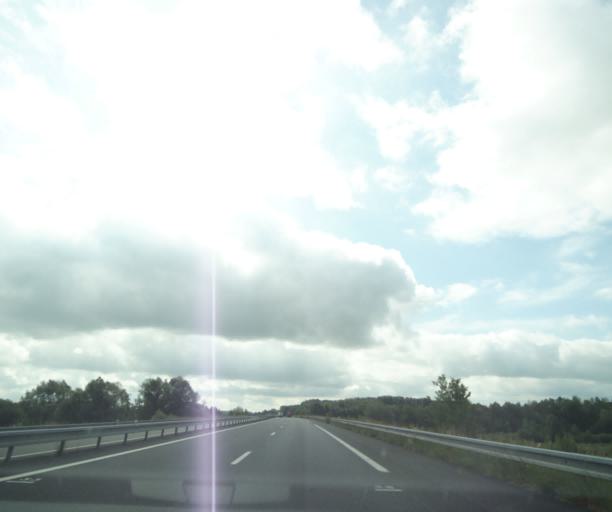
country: FR
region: Pays de la Loire
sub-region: Departement de Maine-et-Loire
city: Vivy
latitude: 47.3427
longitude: -0.0651
